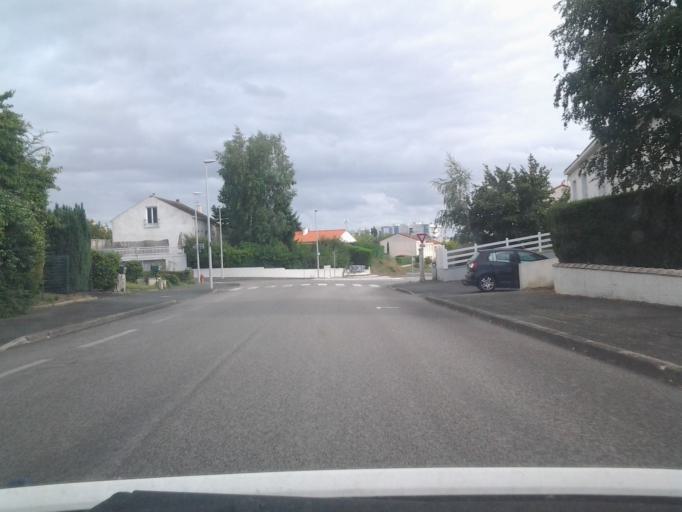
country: FR
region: Pays de la Loire
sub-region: Departement de la Vendee
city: La Roche-sur-Yon
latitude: 46.6836
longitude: -1.4226
